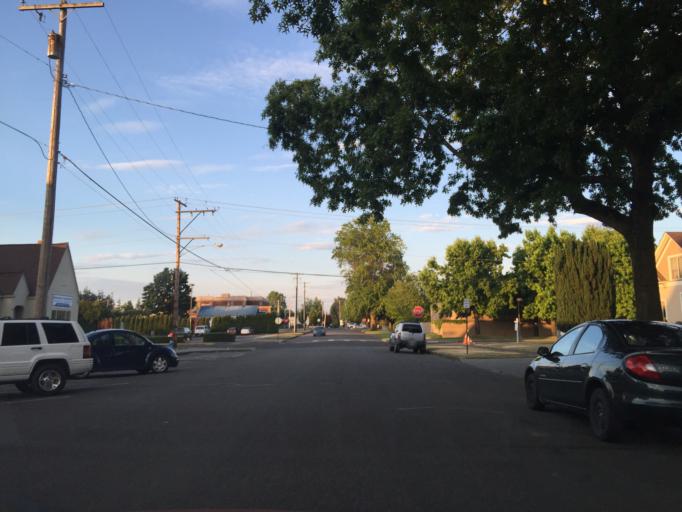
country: US
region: Washington
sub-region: Whatcom County
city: Lynden
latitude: 48.9444
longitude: -122.4551
